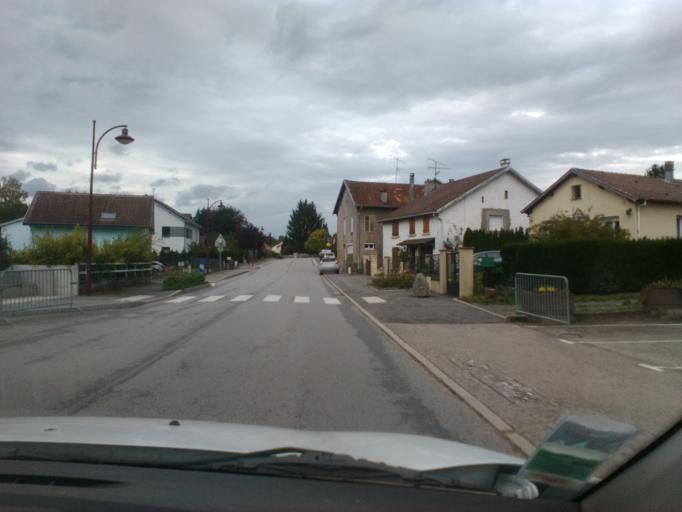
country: FR
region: Lorraine
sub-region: Departement des Vosges
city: Etival-Clairefontaine
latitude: 48.3233
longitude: 6.8268
